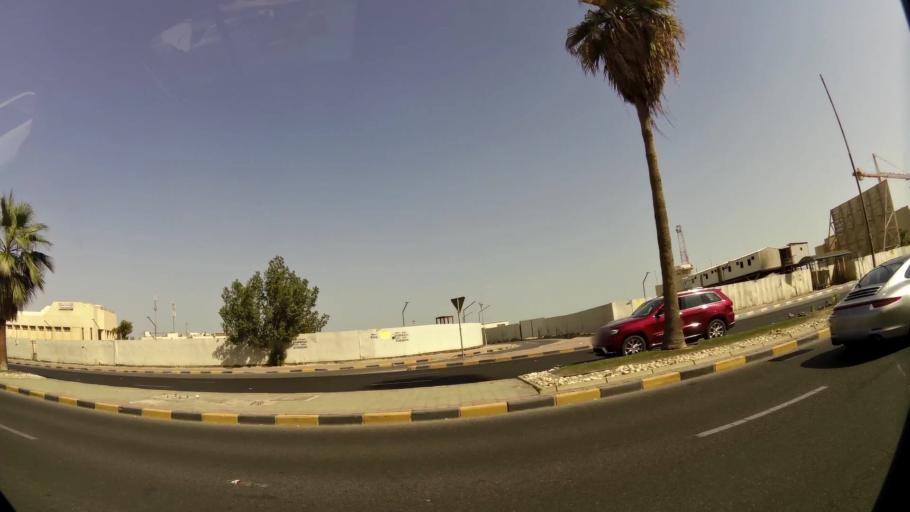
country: KW
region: Muhafazat Hawalli
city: As Salimiyah
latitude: 29.3441
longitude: 48.0965
